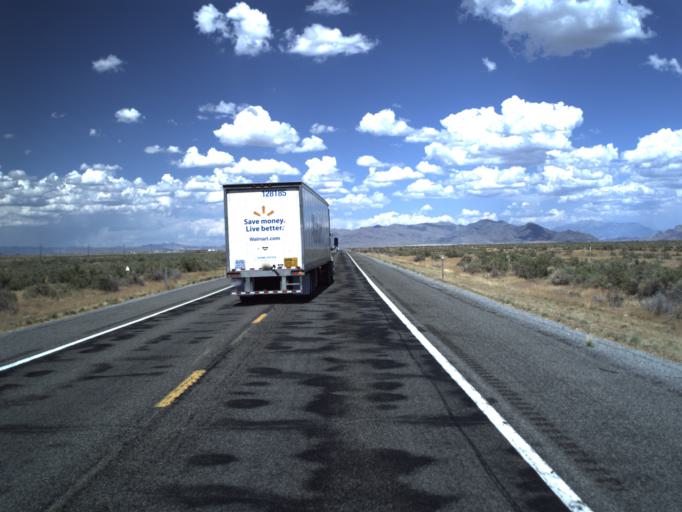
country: US
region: Utah
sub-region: Millard County
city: Delta
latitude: 39.4361
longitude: -112.4605
